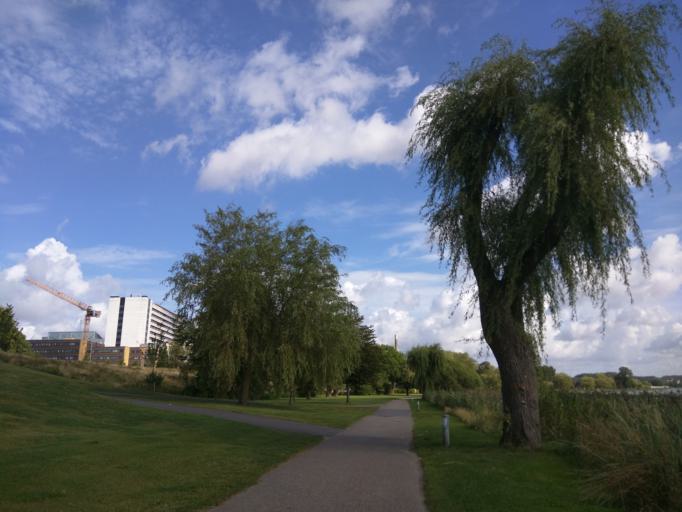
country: DK
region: Central Jutland
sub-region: Viborg Kommune
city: Viborg
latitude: 56.4418
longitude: 9.4050
